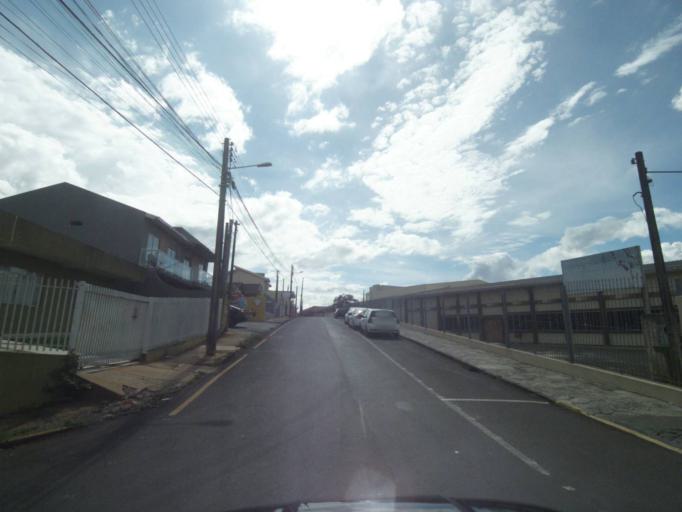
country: BR
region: Parana
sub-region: Telemaco Borba
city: Telemaco Borba
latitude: -24.3230
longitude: -50.6317
